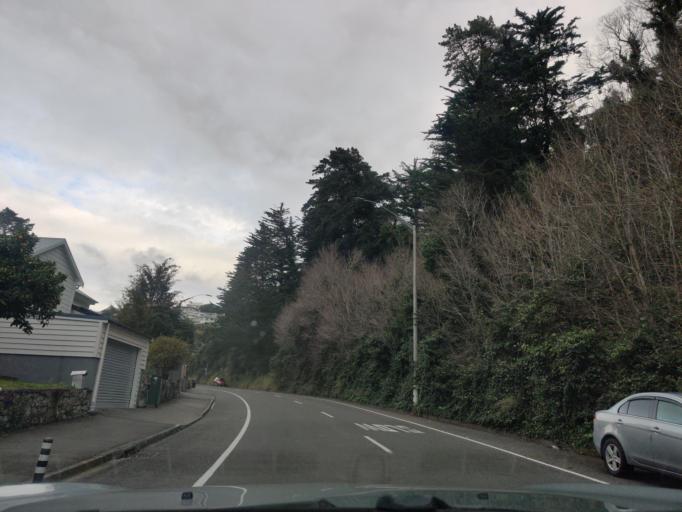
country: NZ
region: Hawke's Bay
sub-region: Napier City
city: Napier
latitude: -39.4819
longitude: 176.9096
